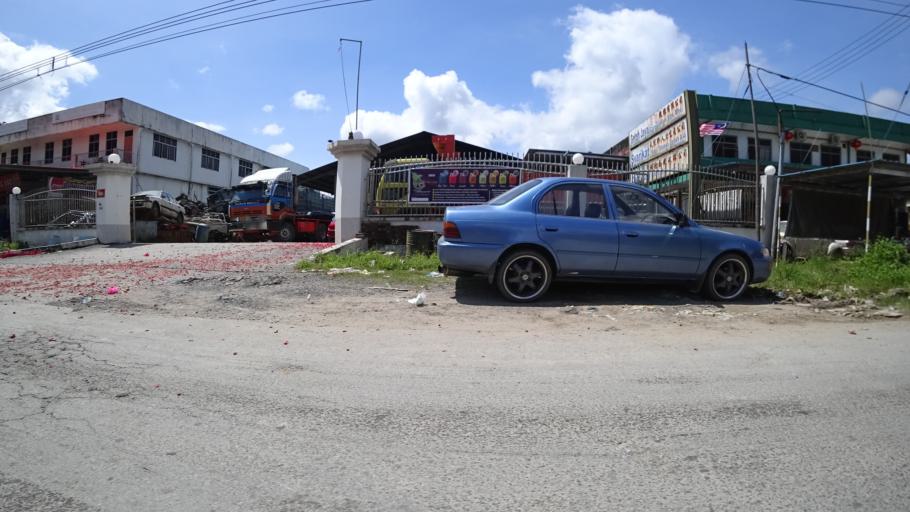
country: MY
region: Sarawak
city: Limbang
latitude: 4.7421
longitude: 115.0019
